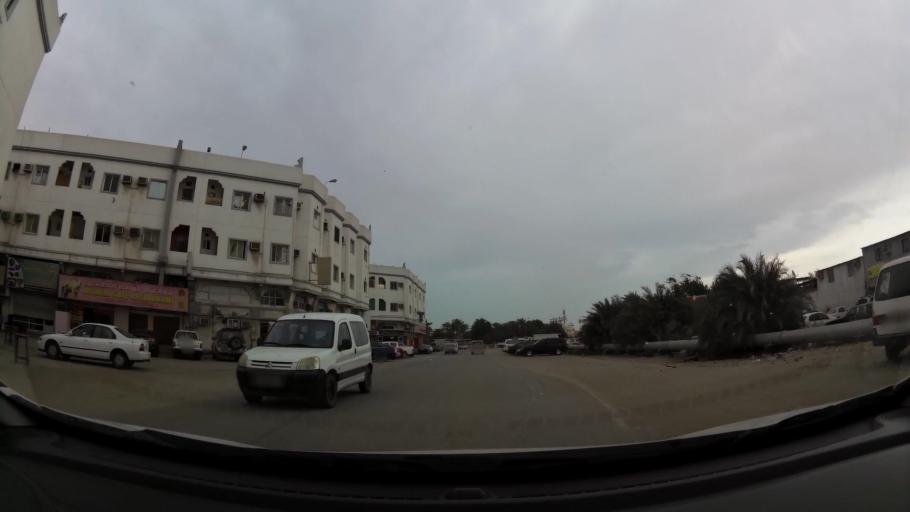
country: BH
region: Central Governorate
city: Madinat Hamad
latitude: 26.1448
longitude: 50.4904
